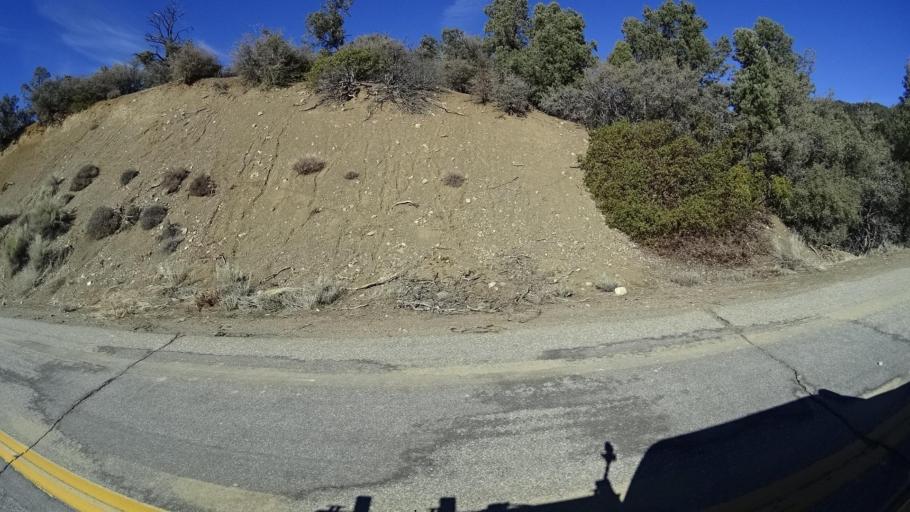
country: US
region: California
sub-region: Kern County
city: Pine Mountain Club
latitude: 34.8654
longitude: -119.2324
